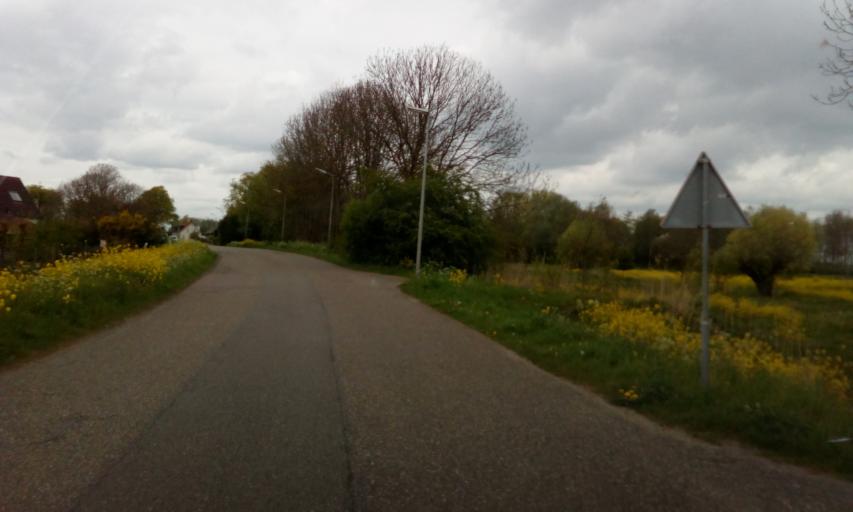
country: NL
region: South Holland
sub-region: Gemeente Zwijndrecht
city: Heerjansdam
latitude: 51.8471
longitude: 4.5690
